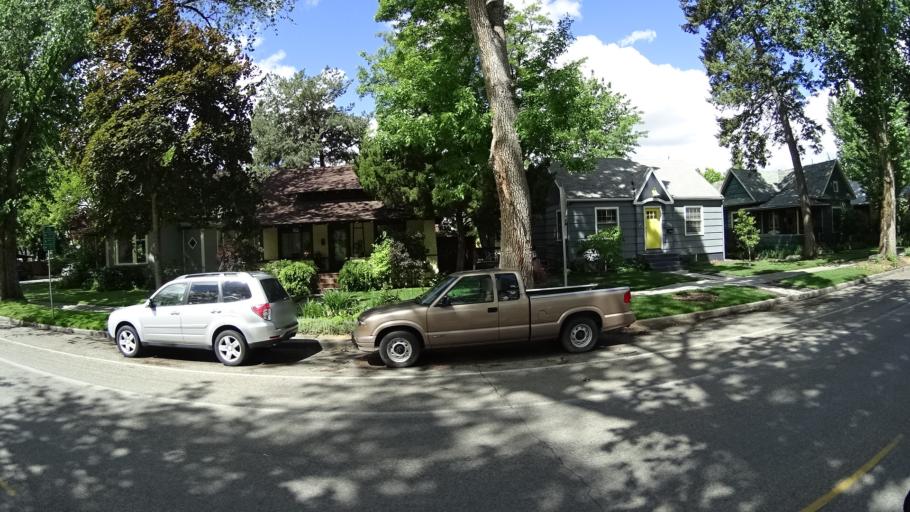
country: US
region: Idaho
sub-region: Ada County
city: Boise
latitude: 43.6305
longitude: -116.2058
